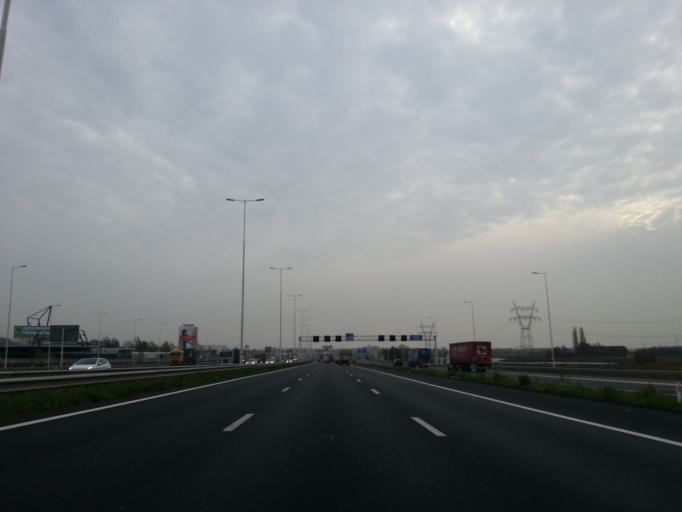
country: NL
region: South Holland
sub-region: Gemeente Albrandswaard
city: Rhoon
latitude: 51.8661
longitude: 4.4481
